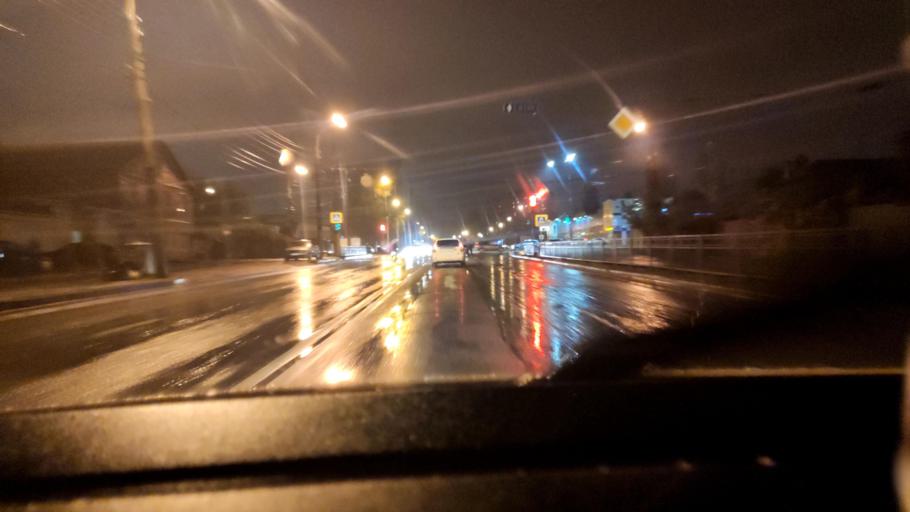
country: RU
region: Voronezj
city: Voronezh
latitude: 51.6430
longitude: 39.1543
